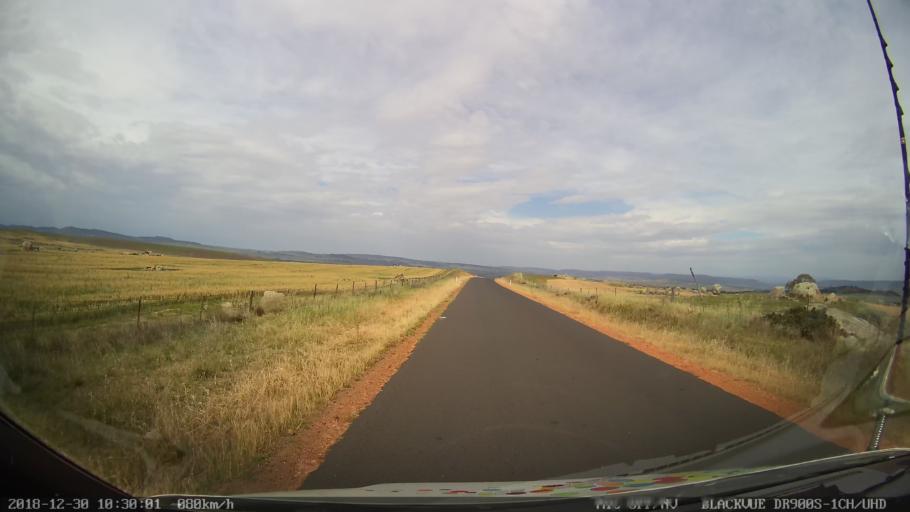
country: AU
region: New South Wales
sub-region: Snowy River
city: Berridale
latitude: -36.5023
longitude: 148.9010
